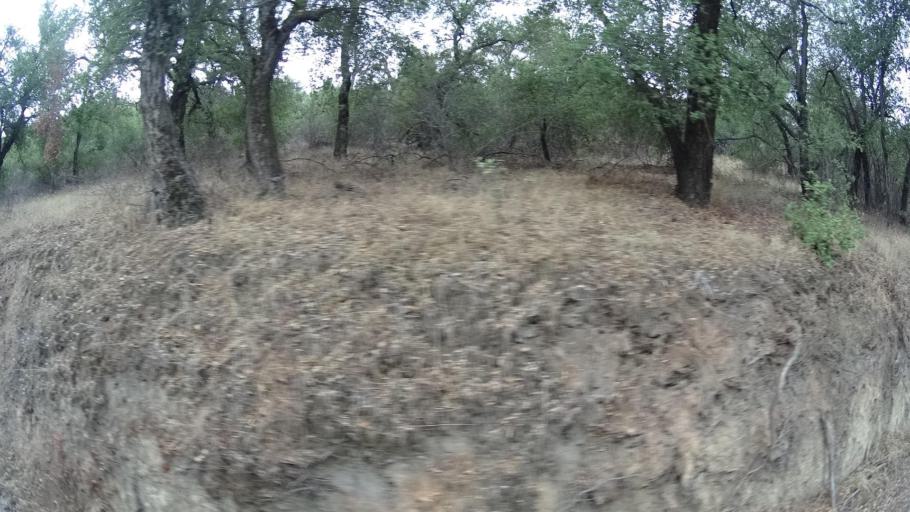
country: US
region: California
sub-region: San Diego County
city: Descanso
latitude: 32.9604
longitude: -116.6583
